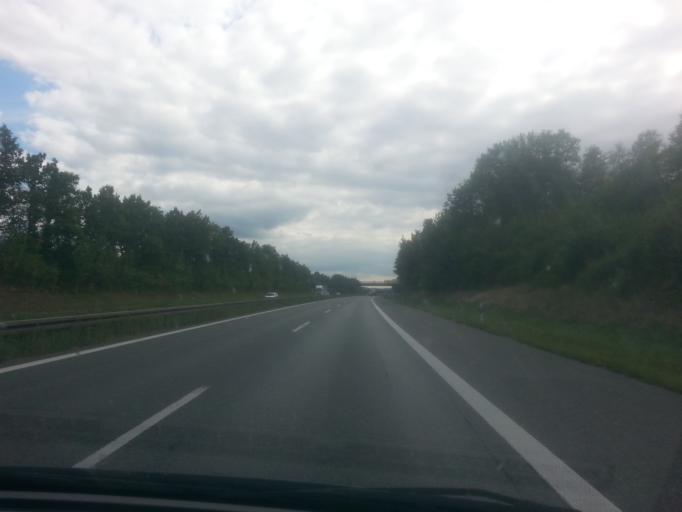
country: DE
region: Bavaria
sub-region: Upper Palatinate
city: Wackersdorf
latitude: 49.3257
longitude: 12.1539
